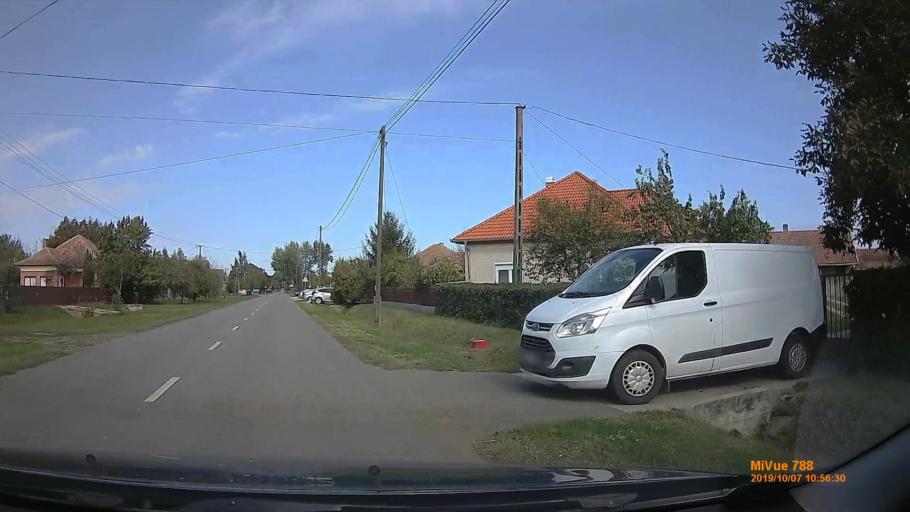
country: HU
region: Bekes
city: Kondoros
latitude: 46.7489
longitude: 20.8016
